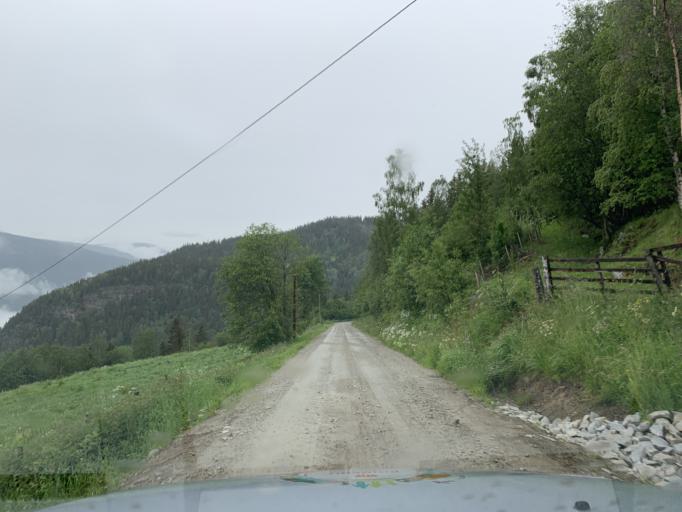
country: NO
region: Oppland
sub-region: Oyer
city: Tretten
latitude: 61.3873
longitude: 10.2817
